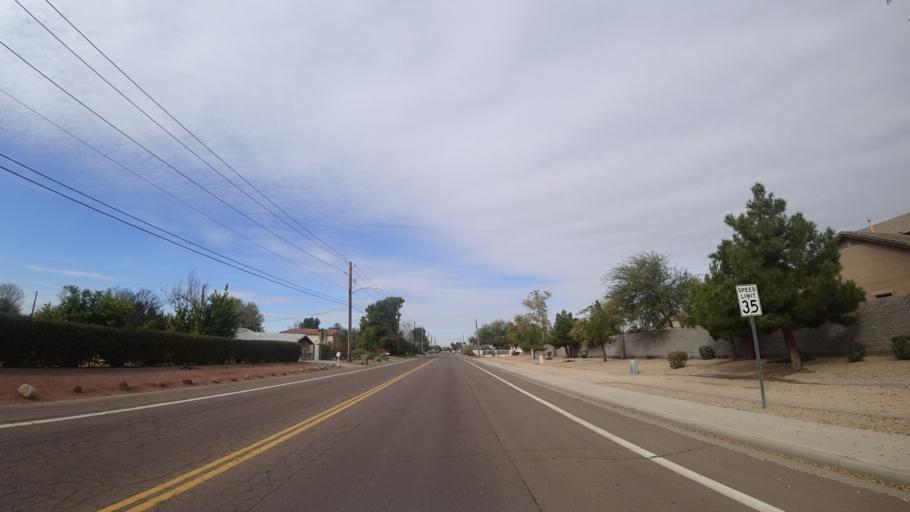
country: US
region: Arizona
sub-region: Maricopa County
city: Peoria
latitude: 33.6619
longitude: -112.1488
